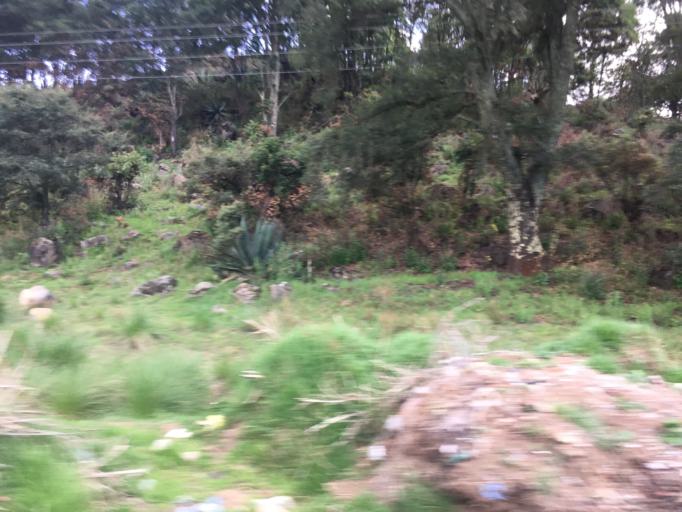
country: MX
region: Mexico
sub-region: Atlacomulco
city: Santiago Acutzilapan
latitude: 19.7835
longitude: -99.7431
